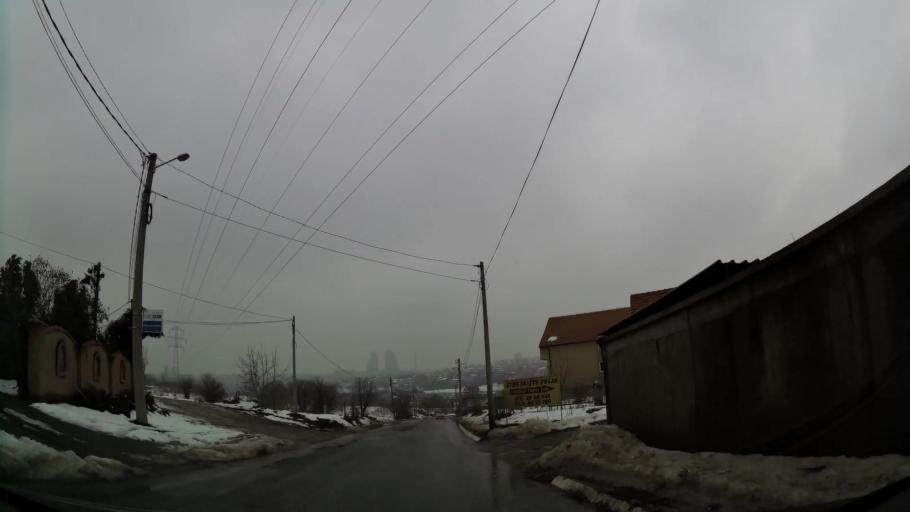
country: RS
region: Central Serbia
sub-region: Belgrade
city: Zvezdara
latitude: 44.7698
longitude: 20.5173
